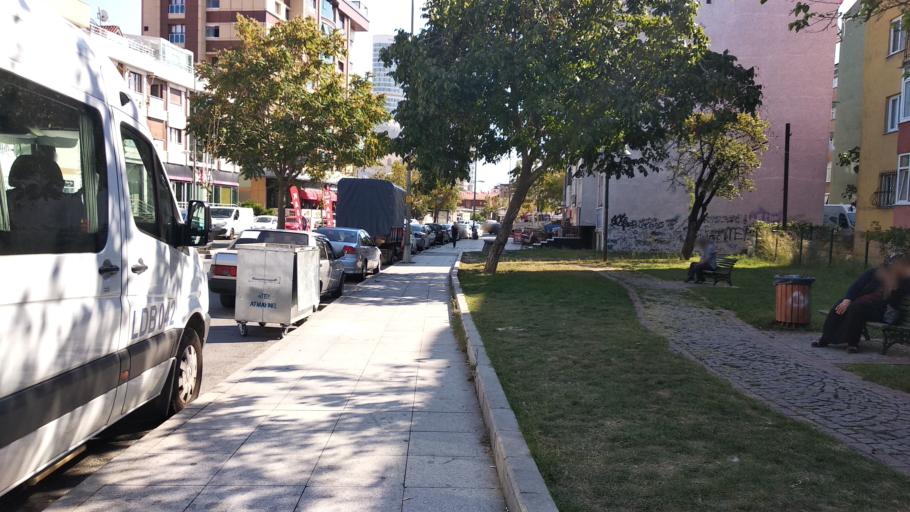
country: TR
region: Istanbul
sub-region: Atasehir
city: Atasehir
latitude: 40.9969
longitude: 29.0823
